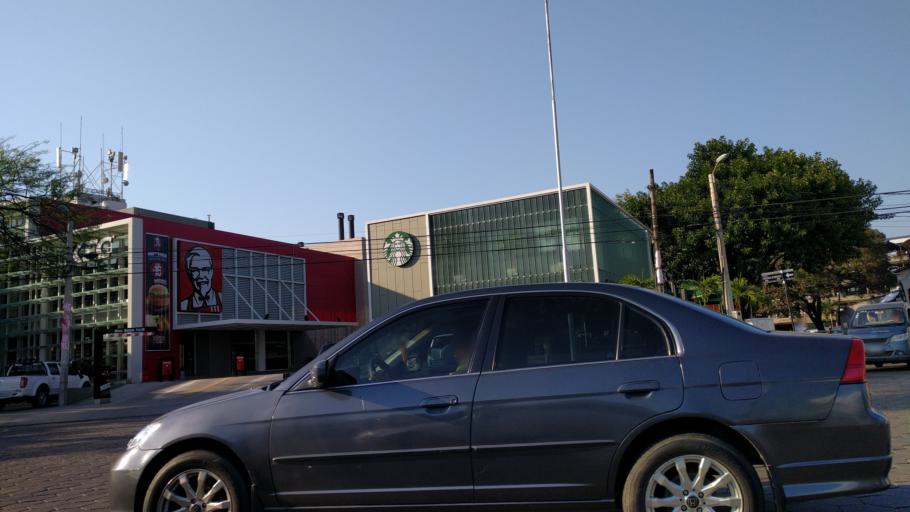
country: BO
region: Santa Cruz
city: Santa Cruz de la Sierra
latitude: -17.7720
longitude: -63.1884
